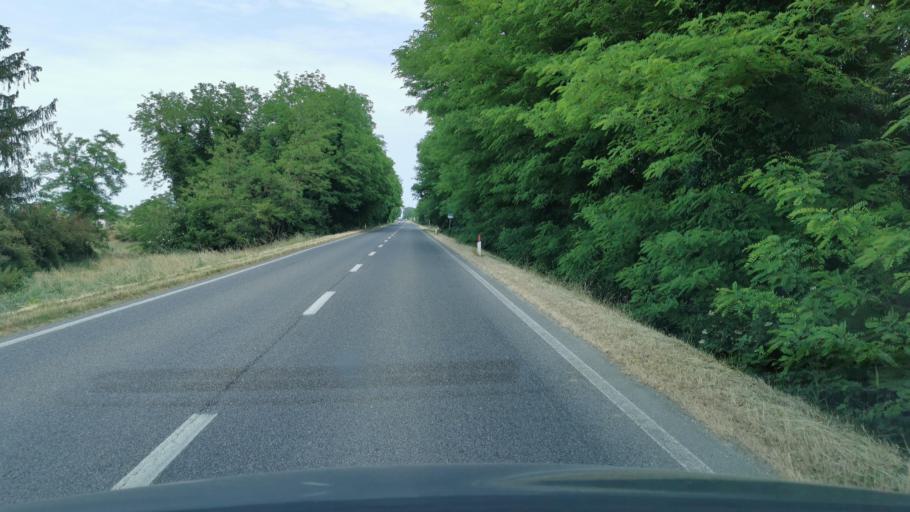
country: IT
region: Emilia-Romagna
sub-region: Provincia di Ravenna
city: Savarna-Conventella
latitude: 44.5305
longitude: 12.1197
